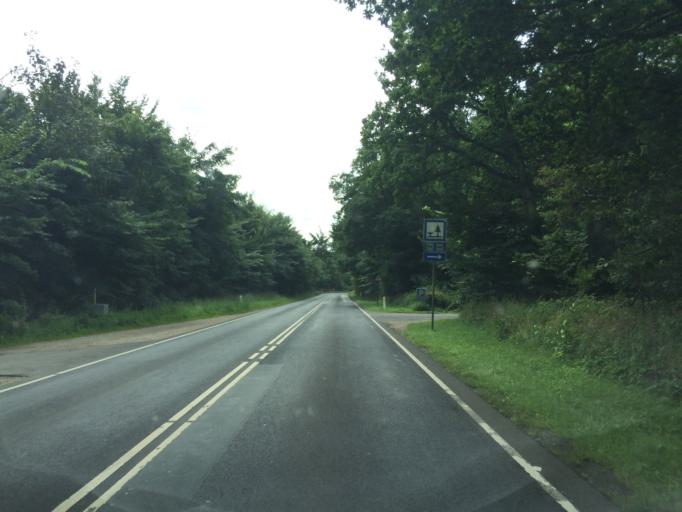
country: DK
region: South Denmark
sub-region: Faaborg-Midtfyn Kommune
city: Faaborg
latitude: 55.1279
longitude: 10.2565
